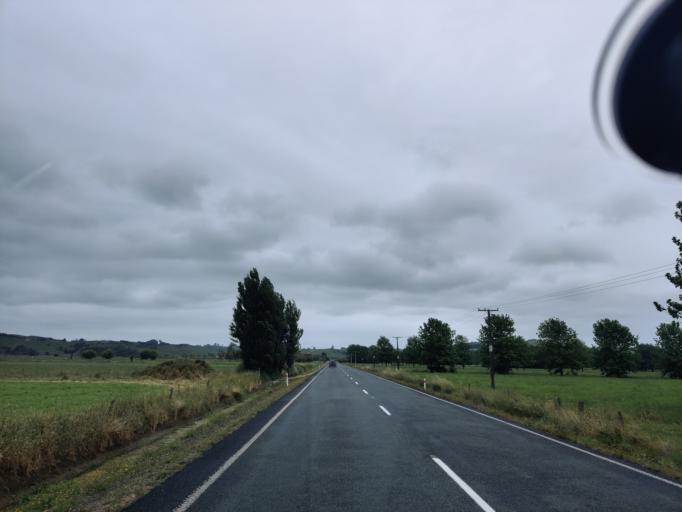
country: NZ
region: Northland
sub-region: Kaipara District
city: Dargaville
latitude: -36.1200
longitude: 174.0857
